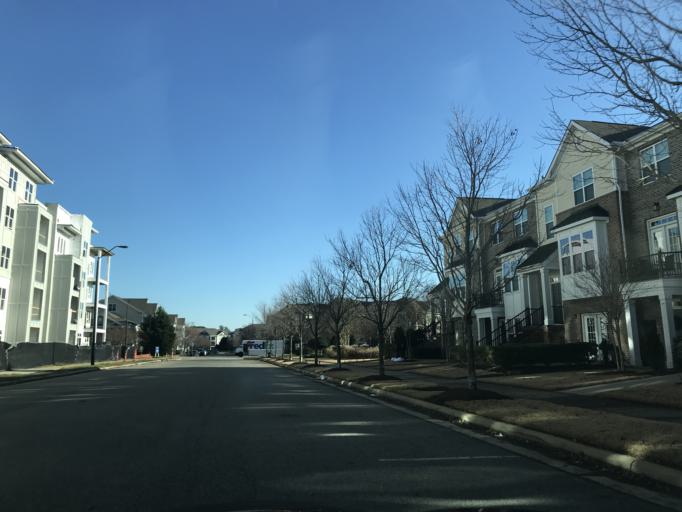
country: US
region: North Carolina
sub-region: Wake County
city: Morrisville
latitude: 35.8996
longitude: -78.7995
